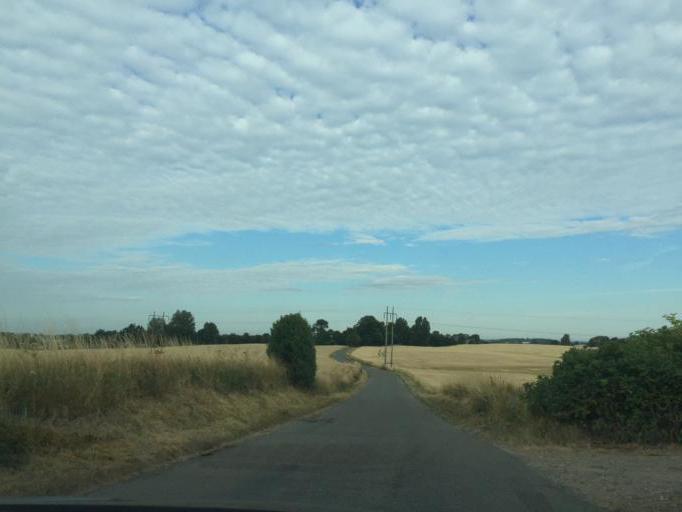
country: DK
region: South Denmark
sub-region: Assens Kommune
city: Assens
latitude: 55.3185
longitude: 9.9708
